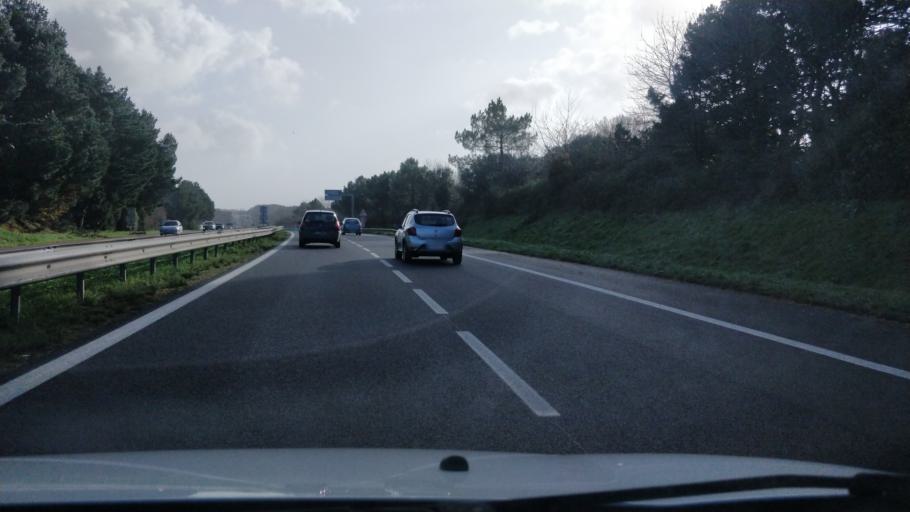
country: FR
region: Pays de la Loire
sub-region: Departement de la Loire-Atlantique
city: Guerande
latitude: 47.3154
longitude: -2.4094
